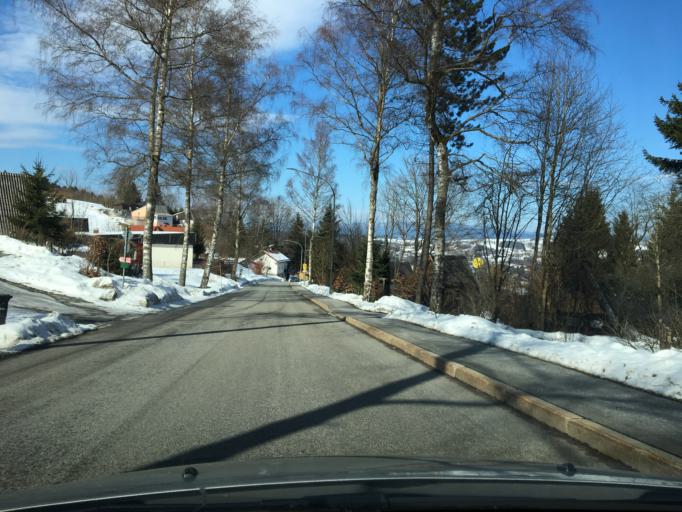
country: DE
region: Bavaria
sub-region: Lower Bavaria
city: Freyung
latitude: 48.7953
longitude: 13.5438
